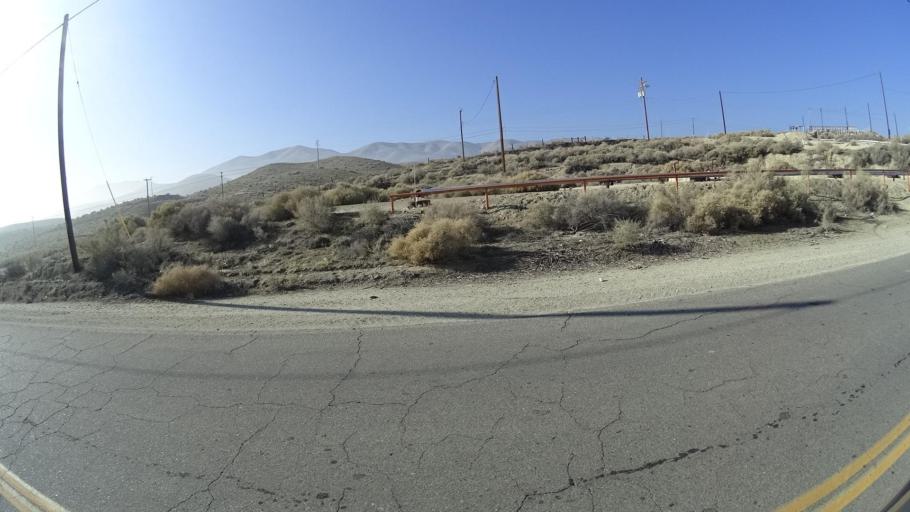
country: US
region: California
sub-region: Kern County
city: Taft Heights
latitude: 35.2007
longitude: -119.5928
